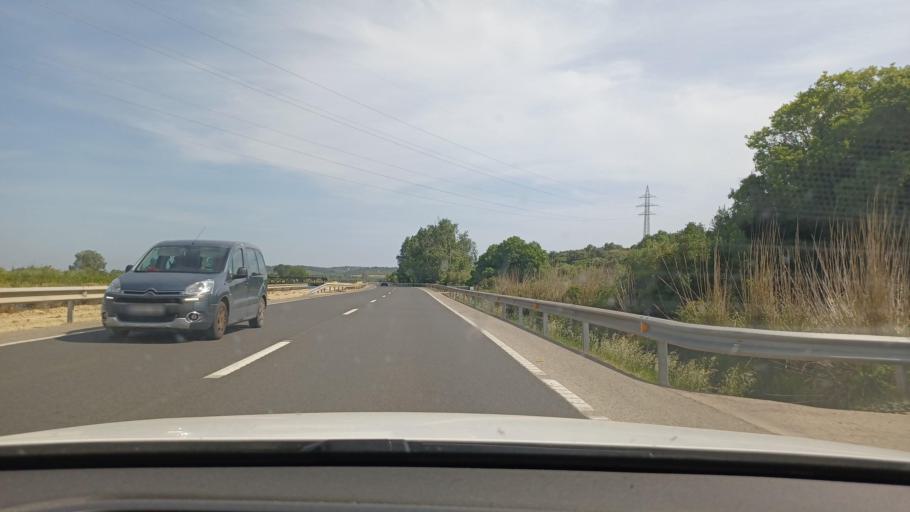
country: ES
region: Catalonia
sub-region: Provincia de Tarragona
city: Masdenverge
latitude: 40.7641
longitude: 0.5328
